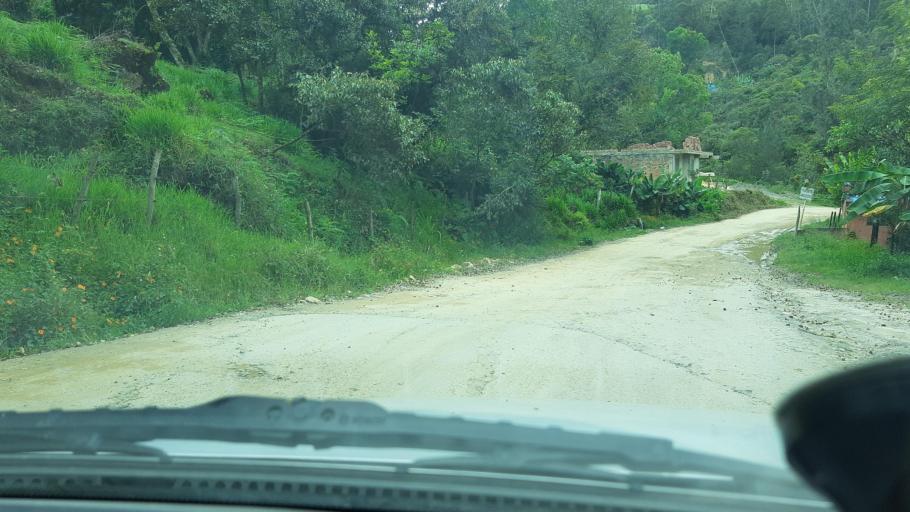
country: CO
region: Cundinamarca
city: Umbita
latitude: 5.2296
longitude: -73.4074
